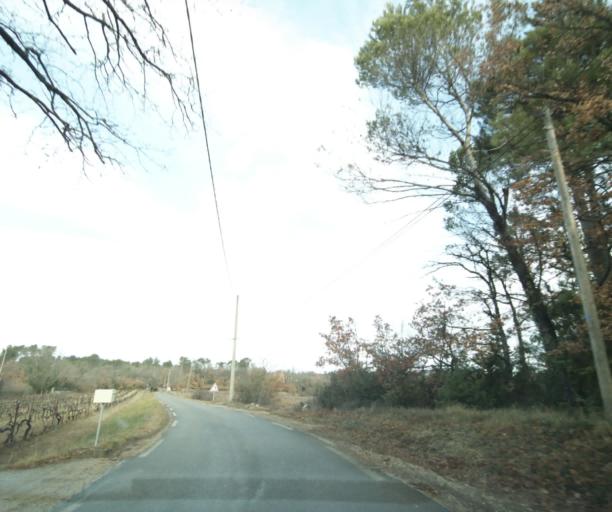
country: FR
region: Provence-Alpes-Cote d'Azur
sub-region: Departement du Var
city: Rougiers
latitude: 43.4075
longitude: 5.8771
